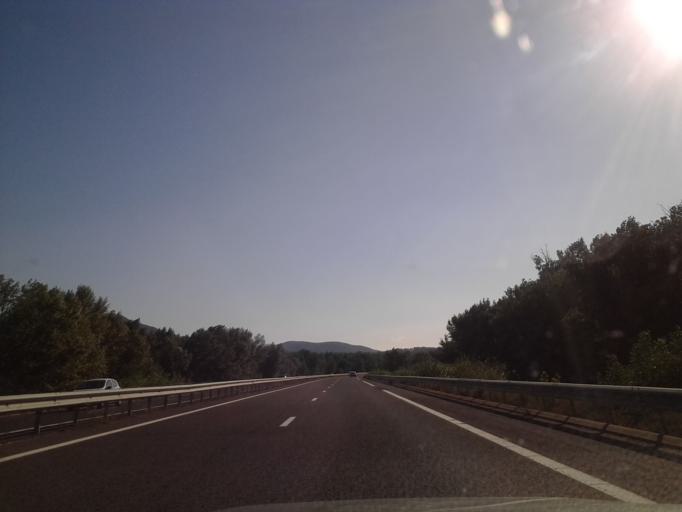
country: FR
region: Languedoc-Roussillon
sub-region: Departement des Pyrenees-Orientales
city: Millas
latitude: 42.6965
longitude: 2.6671
